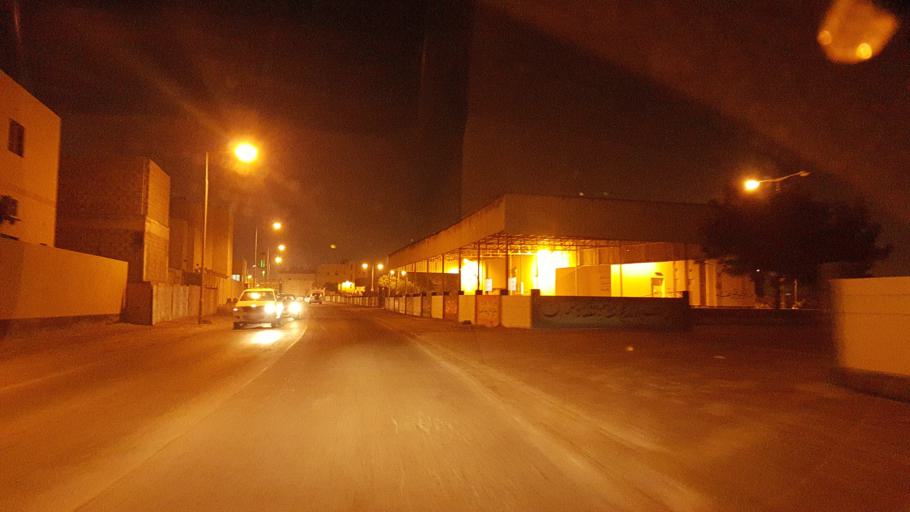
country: BH
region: Manama
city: Jidd Hafs
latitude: 26.2278
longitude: 50.5149
